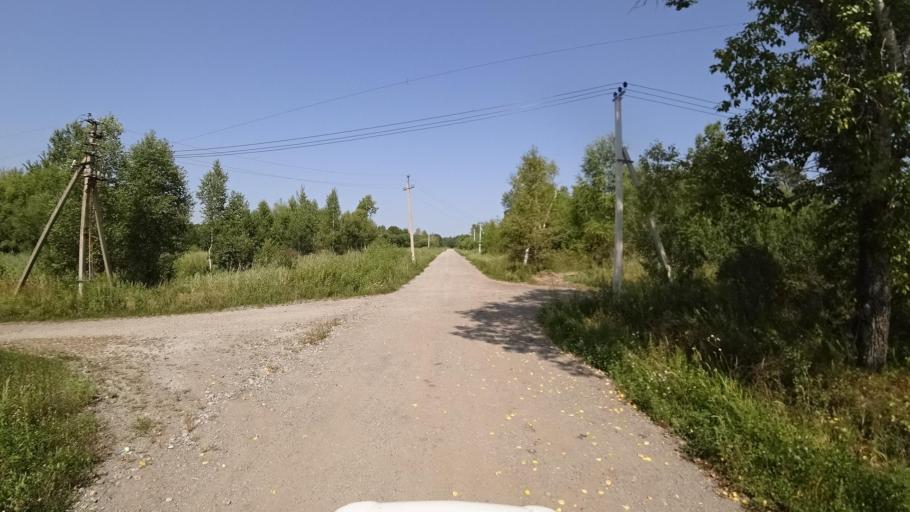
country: RU
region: Khabarovsk Krai
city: Khor
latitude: 47.9678
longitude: 135.1136
